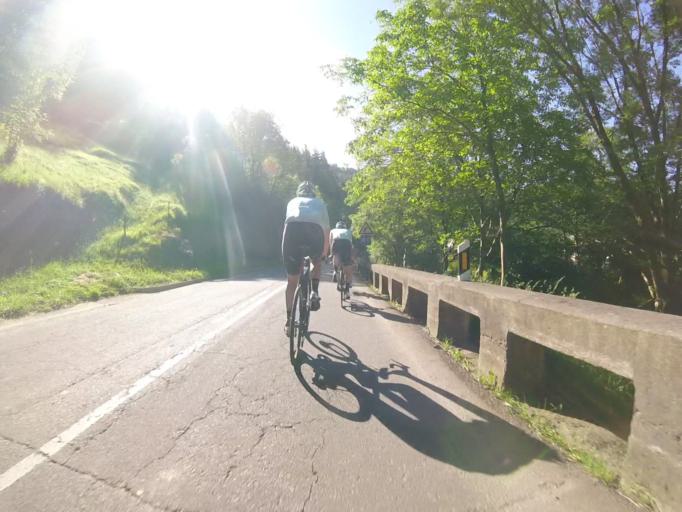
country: ES
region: Basque Country
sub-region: Provincia de Guipuzcoa
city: Beizama
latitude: 43.1472
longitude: -2.2333
